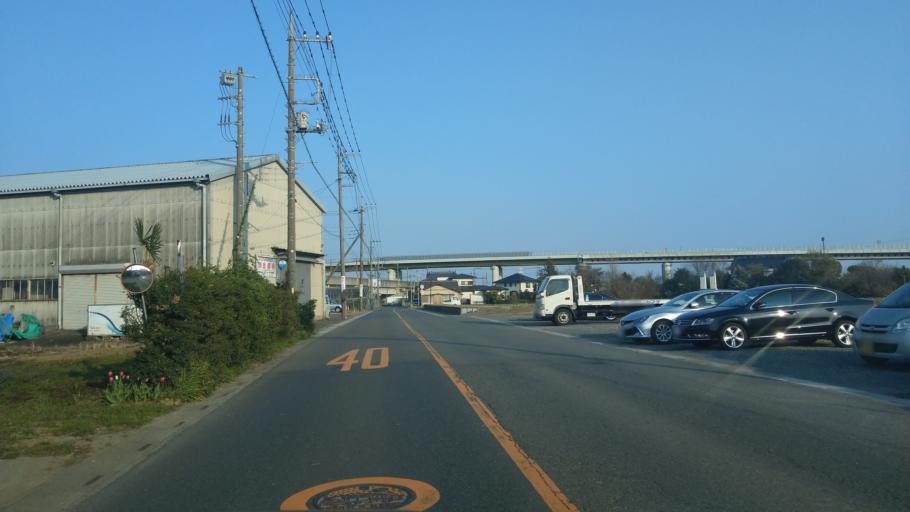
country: JP
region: Saitama
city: Okegawa
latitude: 36.0319
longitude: 139.5755
